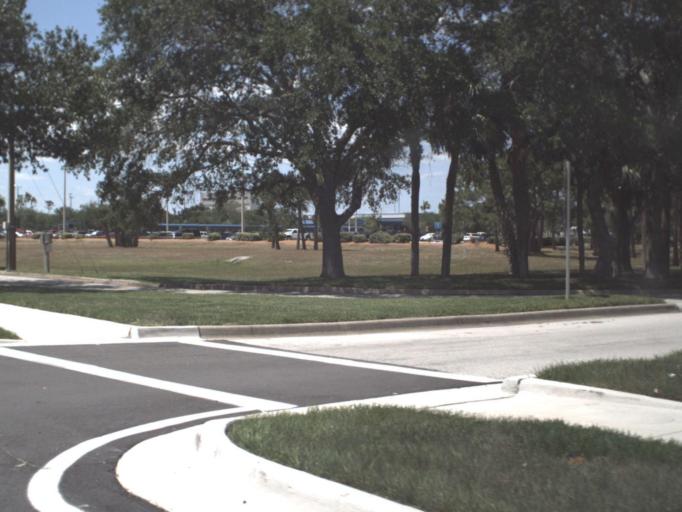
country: US
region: Florida
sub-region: Brevard County
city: Melbourne
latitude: 28.0946
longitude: -80.6281
